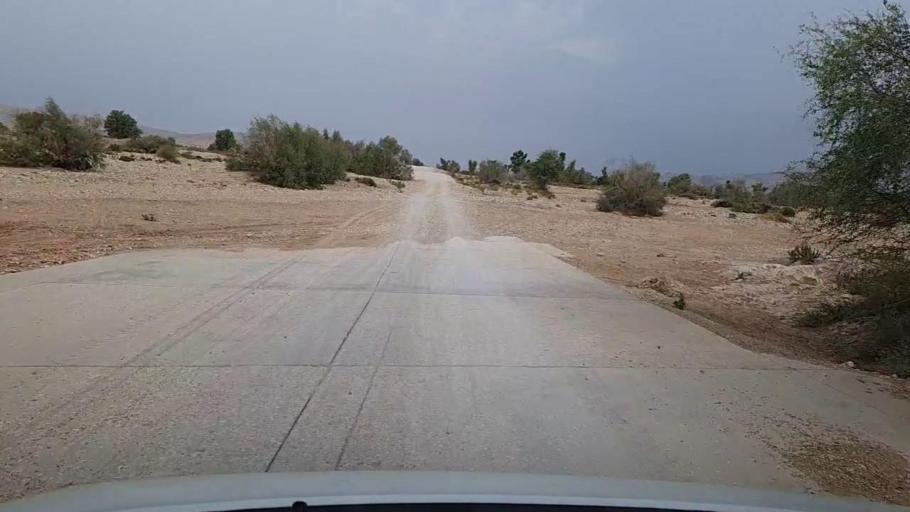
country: PK
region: Sindh
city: Sehwan
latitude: 26.2202
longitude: 67.7145
